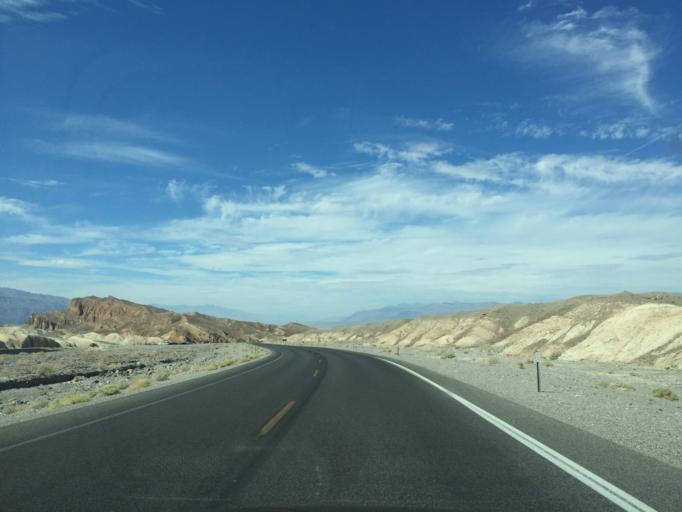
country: US
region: Nevada
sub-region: Nye County
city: Beatty
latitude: 36.4179
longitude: -116.8052
